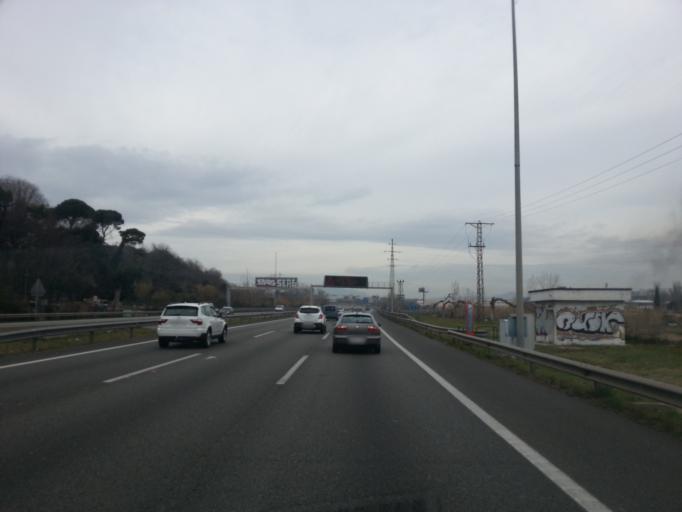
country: ES
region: Catalonia
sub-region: Provincia de Barcelona
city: Ripollet
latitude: 41.4957
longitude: 2.1495
